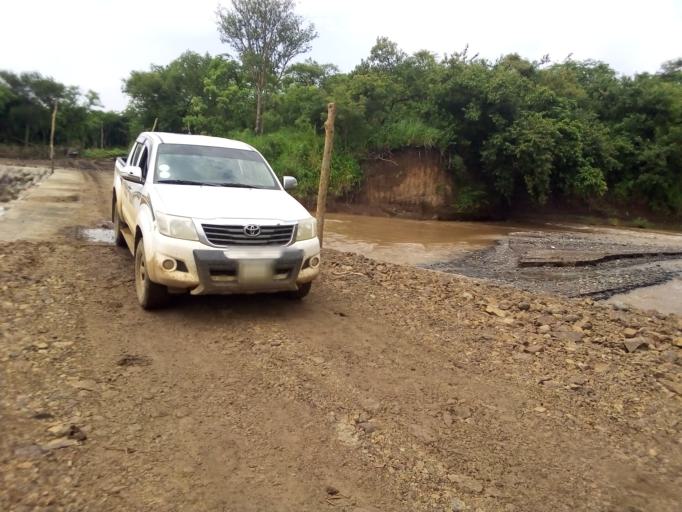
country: ET
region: Oromiya
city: Jima
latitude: 7.2100
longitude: 37.1433
